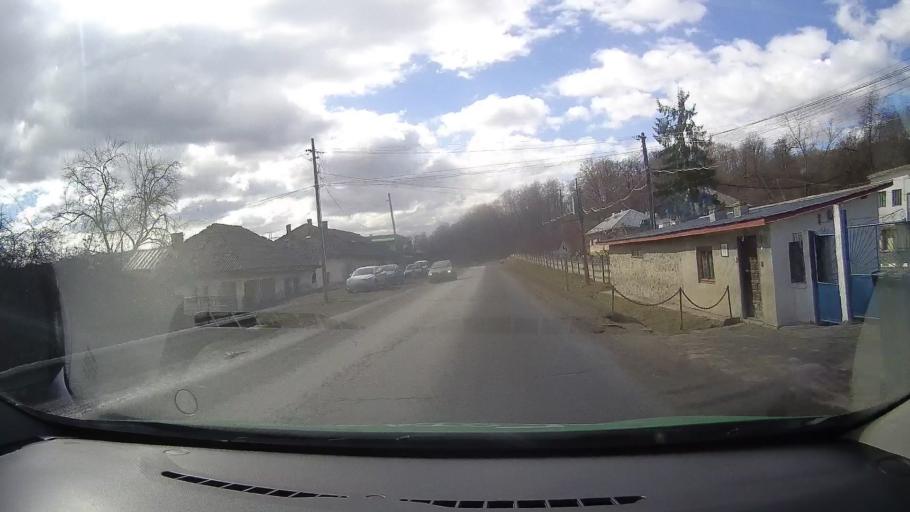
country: RO
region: Dambovita
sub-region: Comuna Buciumeni
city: Buciumeni
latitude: 45.1503
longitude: 25.4455
